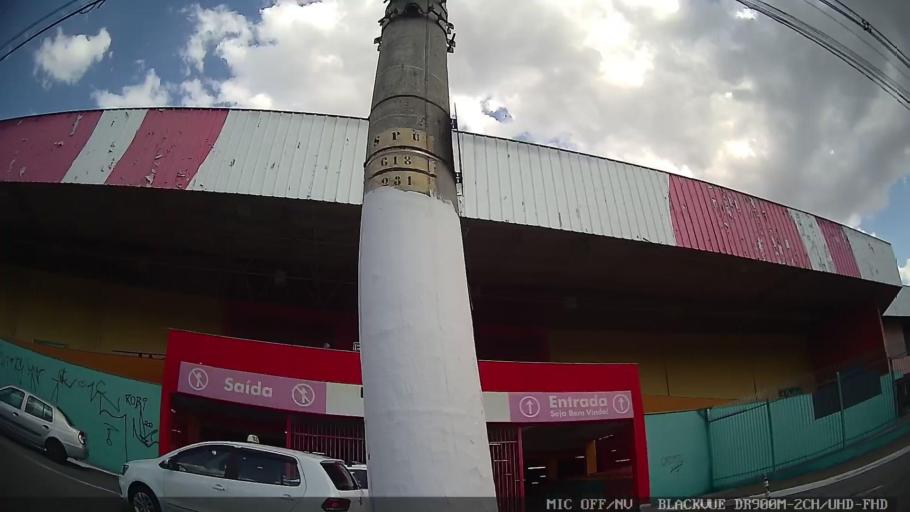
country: BR
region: Sao Paulo
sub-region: Guarulhos
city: Guarulhos
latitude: -23.4983
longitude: -46.4554
